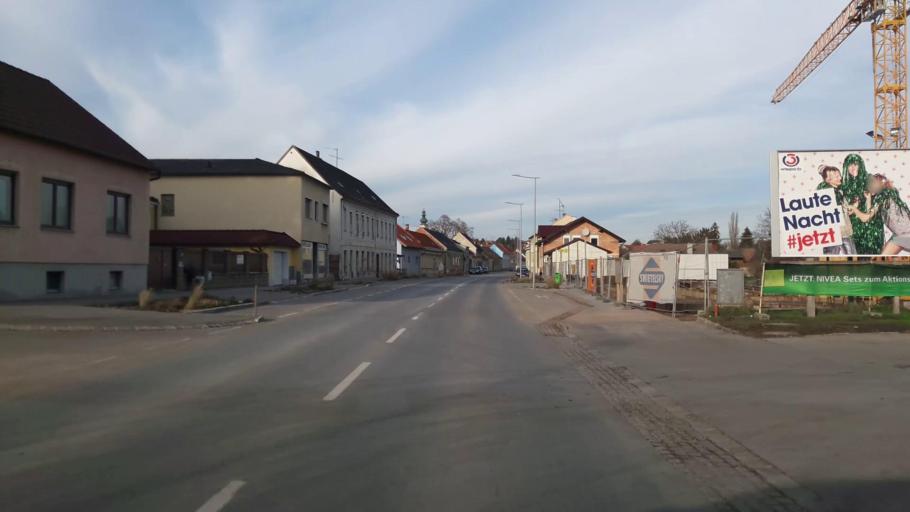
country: AT
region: Lower Austria
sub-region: Politischer Bezirk Mistelbach
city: Gaweinstal
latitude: 48.4725
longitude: 16.5888
